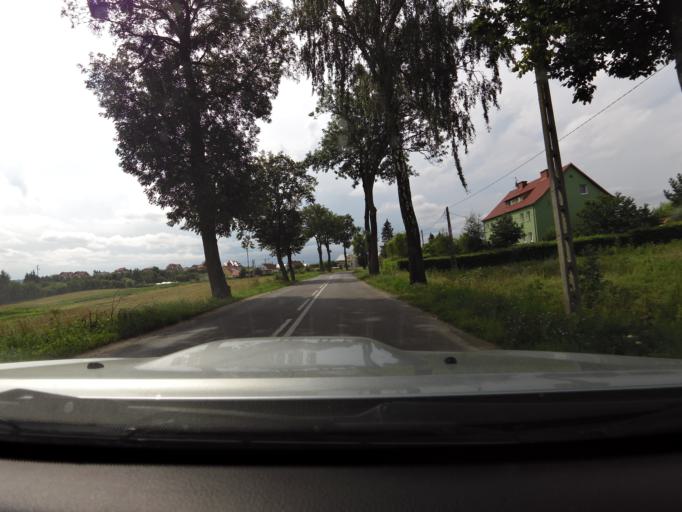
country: PL
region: Warmian-Masurian Voivodeship
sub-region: Powiat ketrzynski
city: Ketrzyn
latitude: 54.0770
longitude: 21.3495
